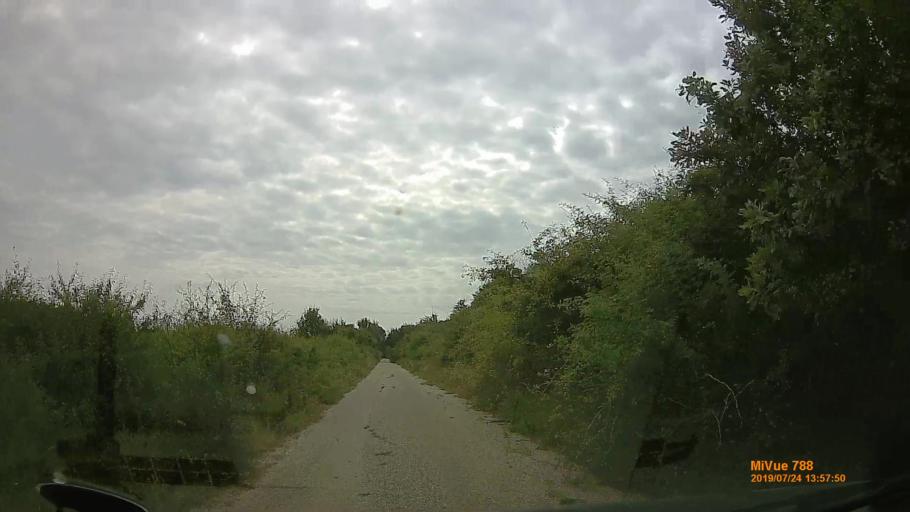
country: HU
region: Szabolcs-Szatmar-Bereg
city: Aranyosapati
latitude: 48.2612
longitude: 22.3277
